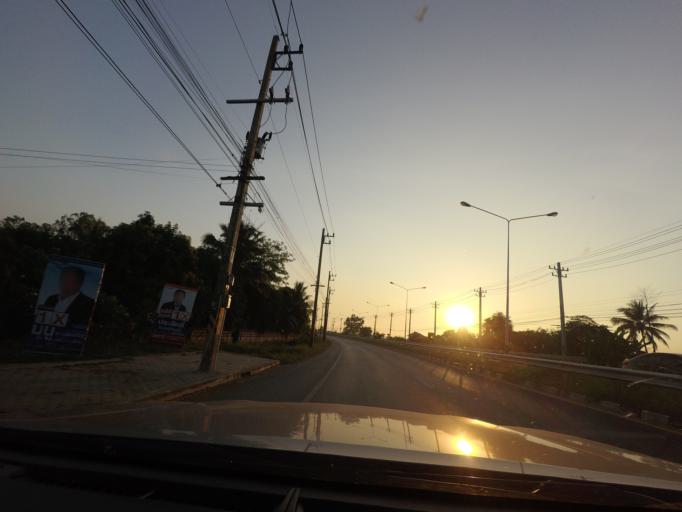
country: TH
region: Sukhothai
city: Si Samrong
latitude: 17.1099
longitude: 99.8438
